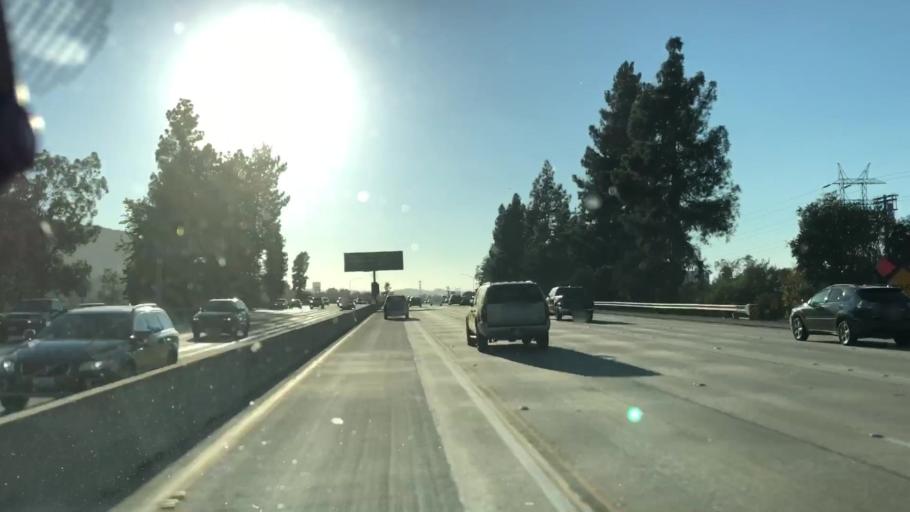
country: US
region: California
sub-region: Los Angeles County
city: Burbank
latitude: 34.1550
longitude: -118.3078
